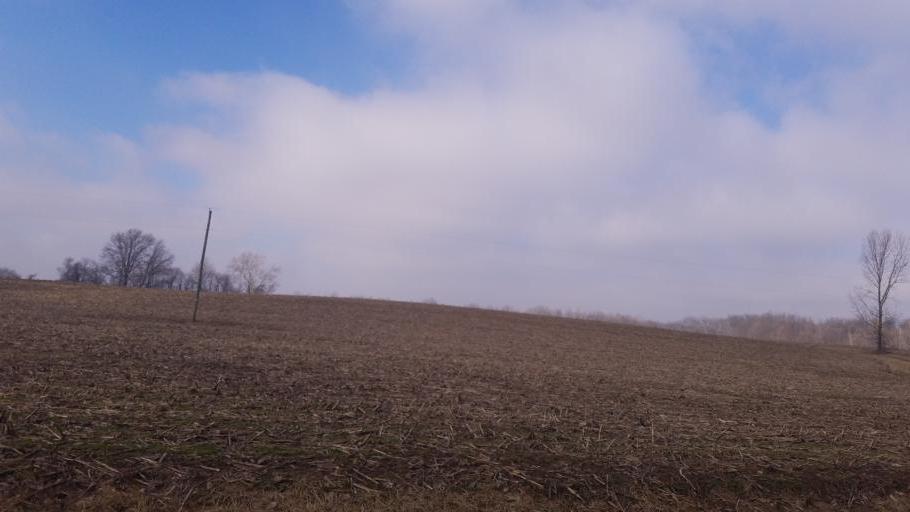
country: US
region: Ohio
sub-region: Crawford County
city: Galion
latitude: 40.6667
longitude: -82.8600
